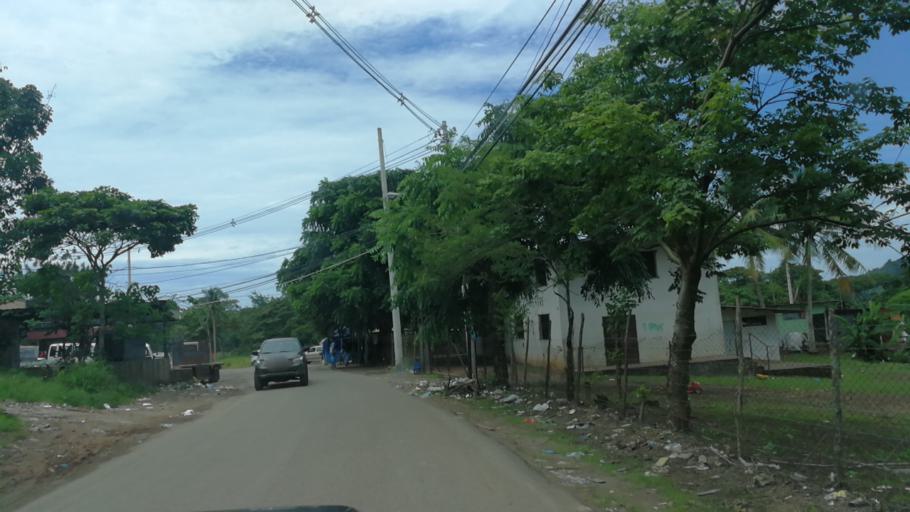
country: PA
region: Panama
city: San Miguelito
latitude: 9.0955
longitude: -79.4561
